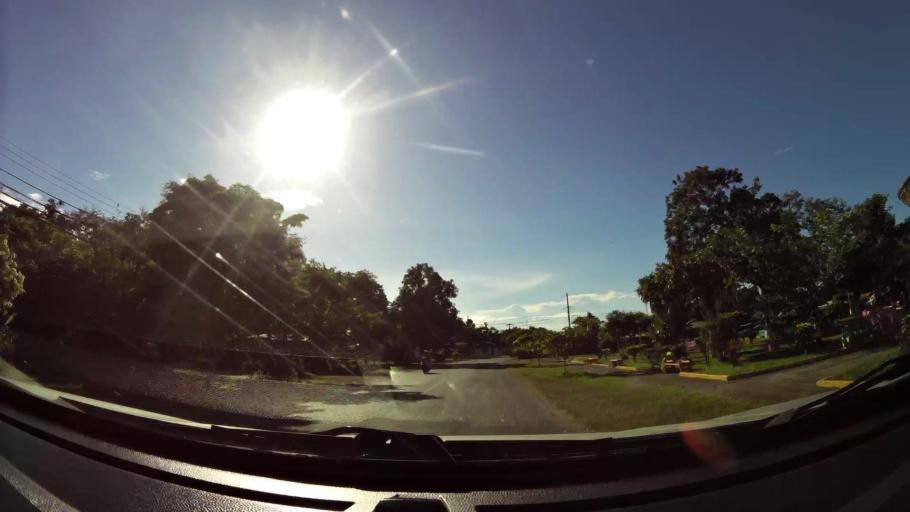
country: CR
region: Guanacaste
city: Belen
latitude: 10.4508
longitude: -85.5535
